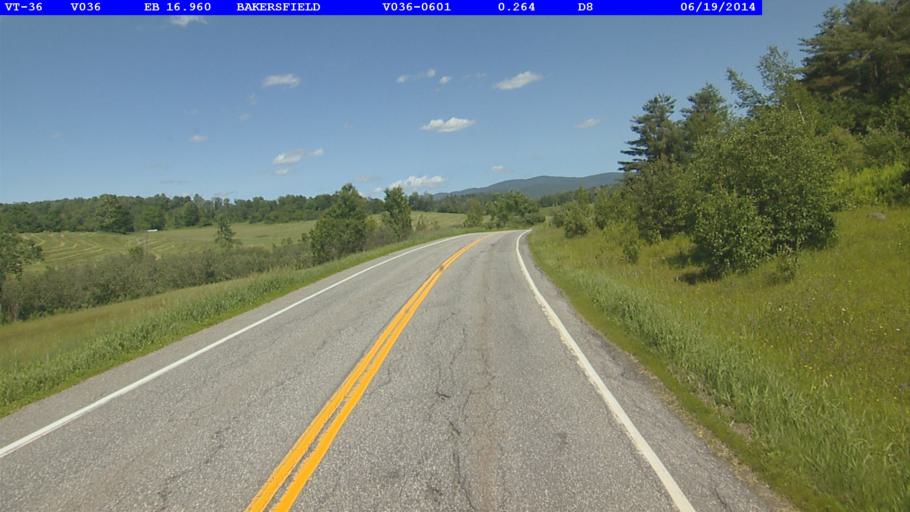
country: US
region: Vermont
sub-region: Franklin County
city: Enosburg Falls
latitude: 44.7853
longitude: -72.8444
